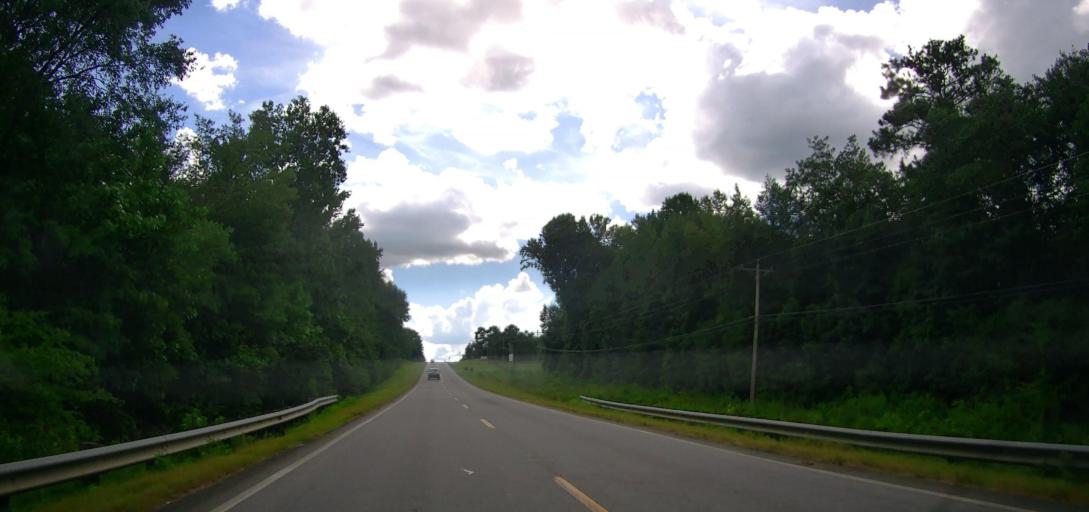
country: US
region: Alabama
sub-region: Russell County
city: Ladonia
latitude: 32.4448
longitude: -85.2737
